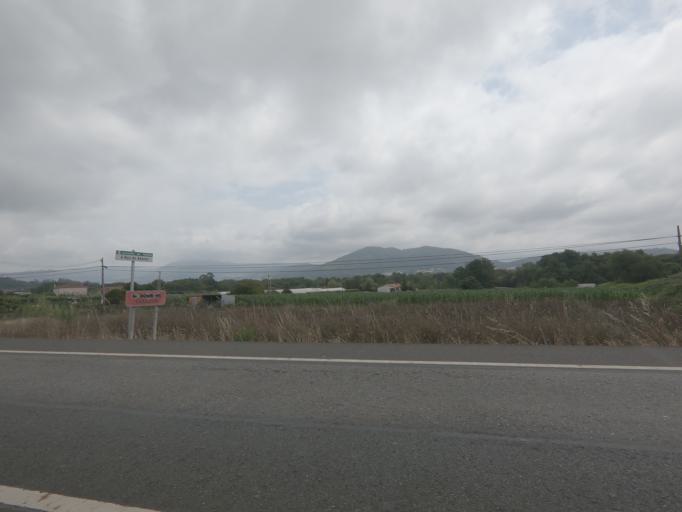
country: ES
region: Galicia
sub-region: Provincia de Pontevedra
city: O Rosal
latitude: 41.9220
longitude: -8.8105
